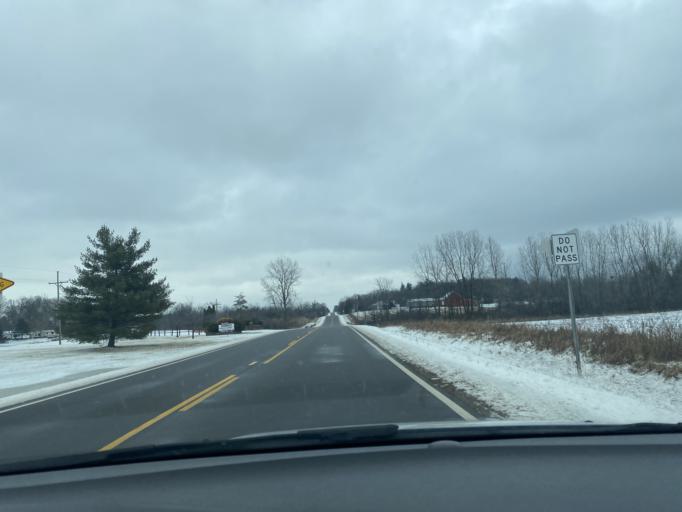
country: US
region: Michigan
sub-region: Lapeer County
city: North Branch
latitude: 43.2068
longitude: -83.2216
